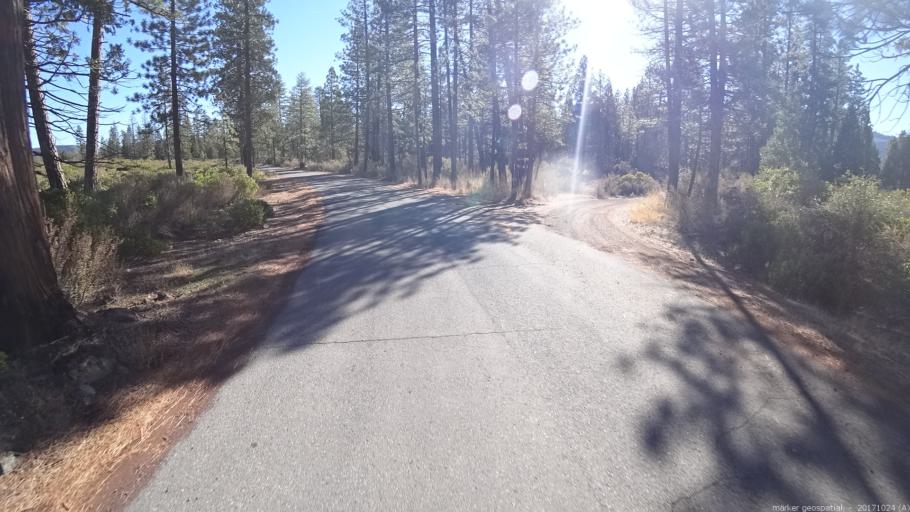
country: US
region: California
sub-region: Shasta County
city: Burney
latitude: 40.7489
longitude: -121.4703
